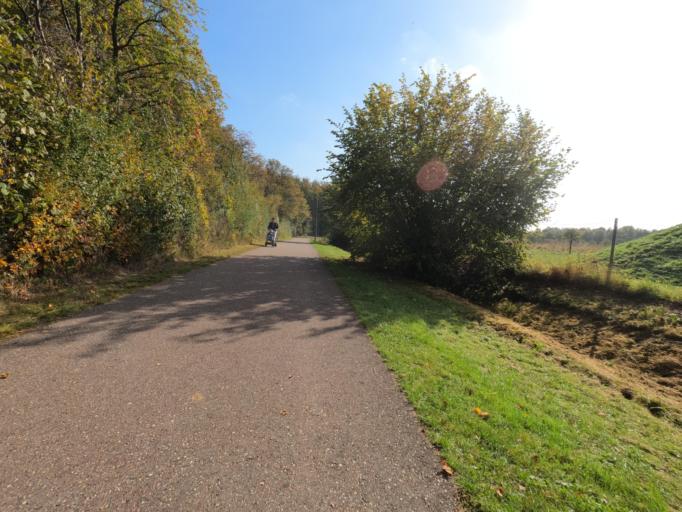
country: DE
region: North Rhine-Westphalia
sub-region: Regierungsbezirk Koln
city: Inden
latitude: 50.8502
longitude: 6.3685
